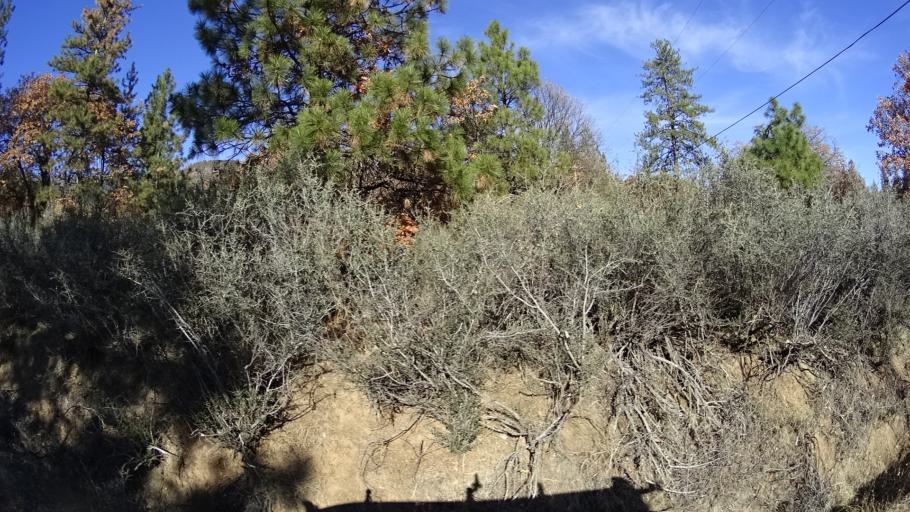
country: US
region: California
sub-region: Siskiyou County
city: Yreka
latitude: 41.7211
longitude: -122.6899
